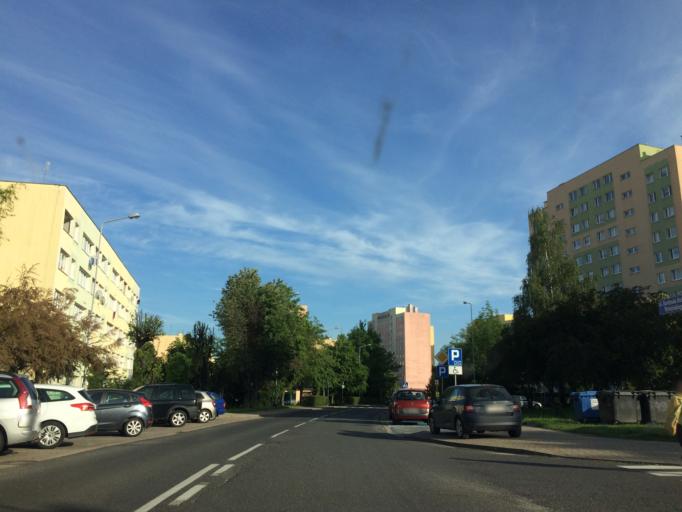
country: PL
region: Lower Silesian Voivodeship
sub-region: Powiat swidnicki
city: Swidnica
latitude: 50.8480
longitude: 16.4672
